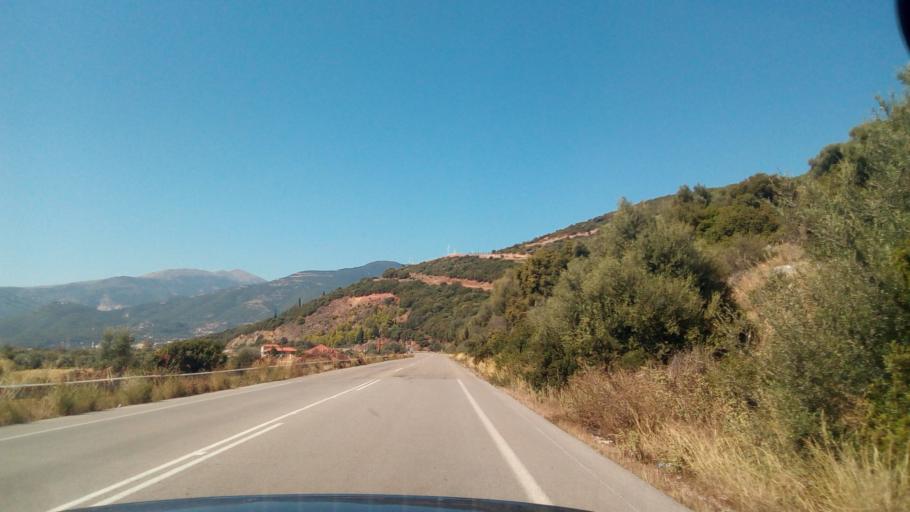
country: GR
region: West Greece
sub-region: Nomos Aitolias kai Akarnanias
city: Nafpaktos
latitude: 38.4049
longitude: 21.9133
